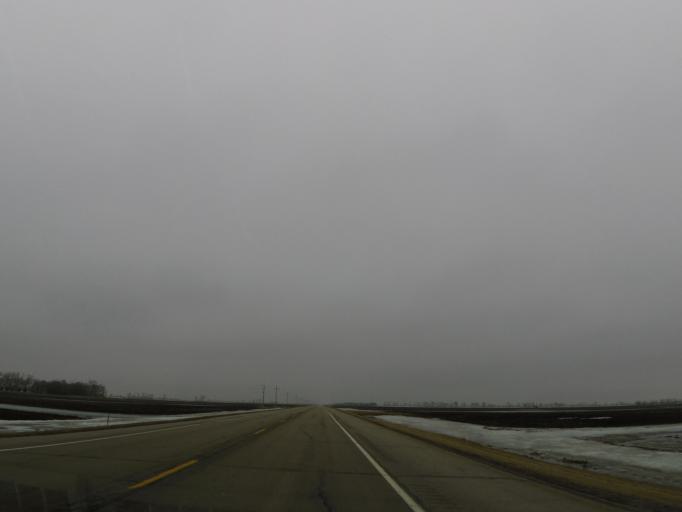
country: US
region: North Dakota
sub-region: Walsh County
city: Grafton
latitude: 48.4119
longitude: -97.2279
